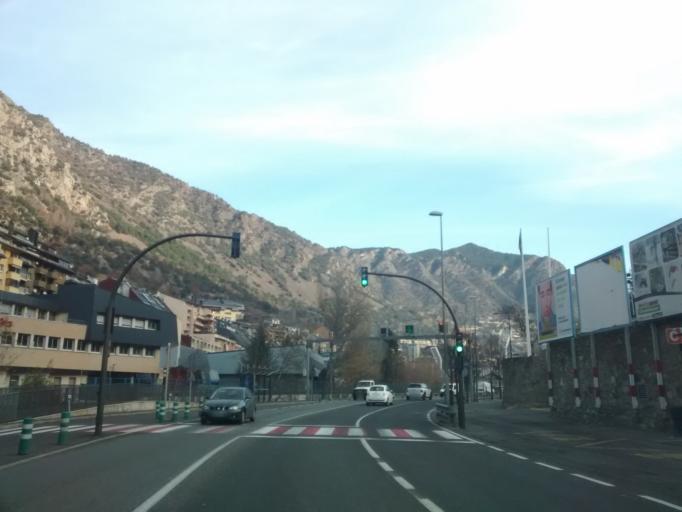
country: AD
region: Andorra la Vella
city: Andorra la Vella
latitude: 42.5017
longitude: 1.5134
